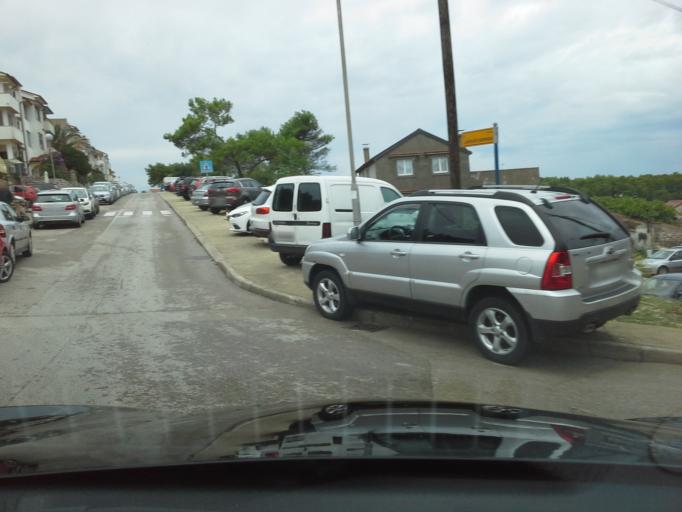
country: HR
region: Primorsko-Goranska
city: Mali Losinj
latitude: 44.5316
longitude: 14.4780
